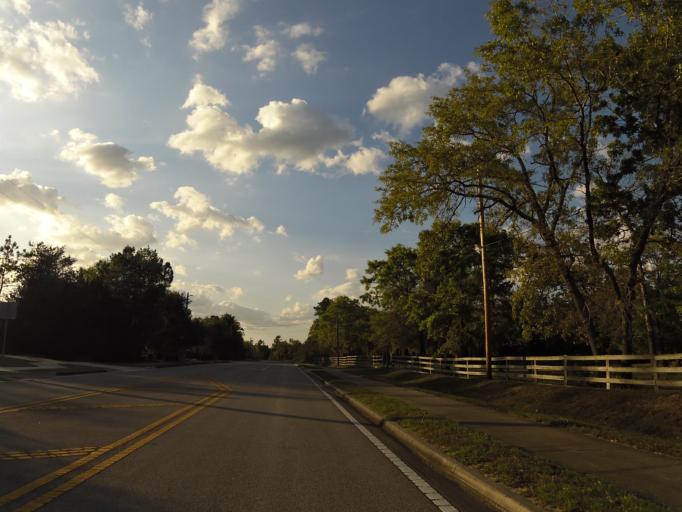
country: US
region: Florida
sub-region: Saint Johns County
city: Fruit Cove
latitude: 30.0734
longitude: -81.5166
